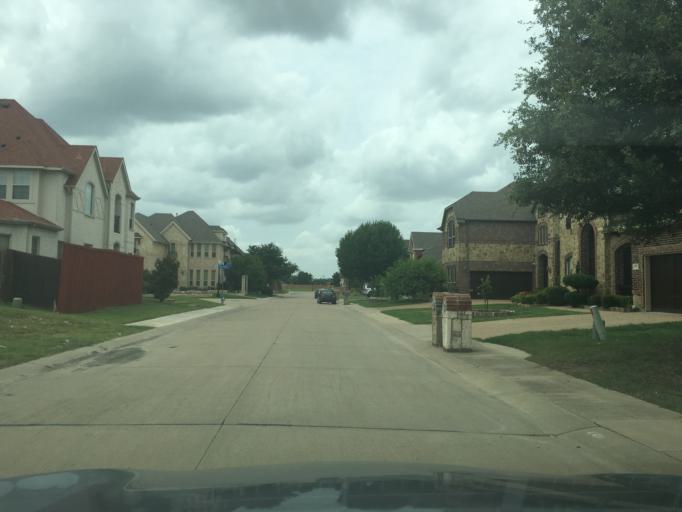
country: US
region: Texas
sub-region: Dallas County
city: Richardson
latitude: 32.9378
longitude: -96.7262
